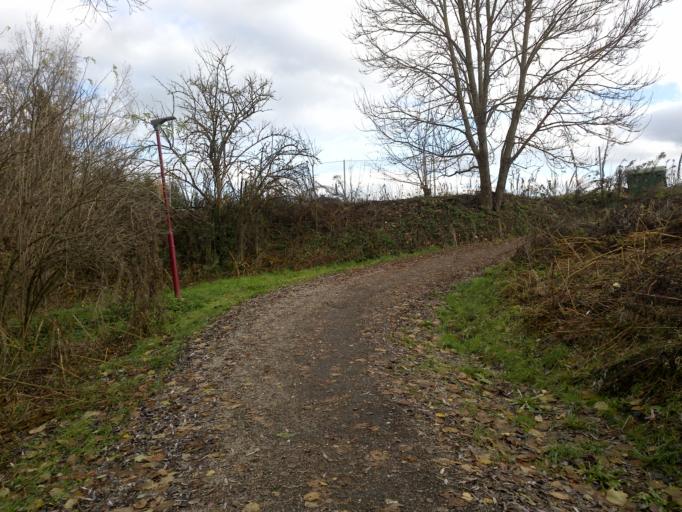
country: AT
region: Styria
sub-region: Politischer Bezirk Murtal
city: Fohnsdorf
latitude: 47.1928
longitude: 14.6756
